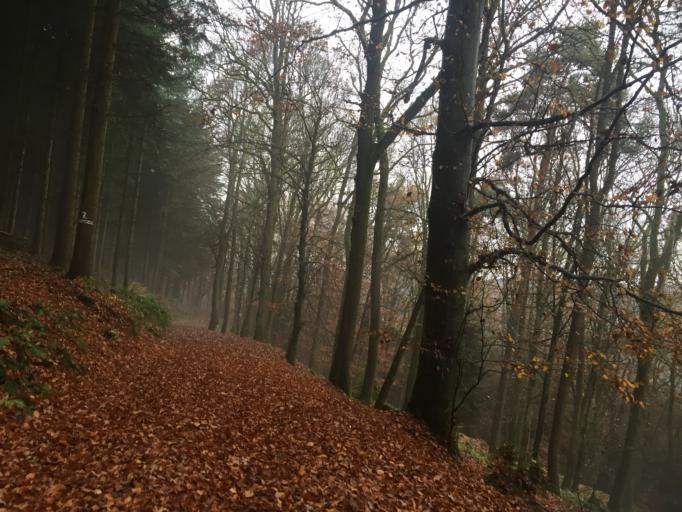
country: DE
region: Hesse
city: Hirschhorn
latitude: 49.4446
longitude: 8.8816
